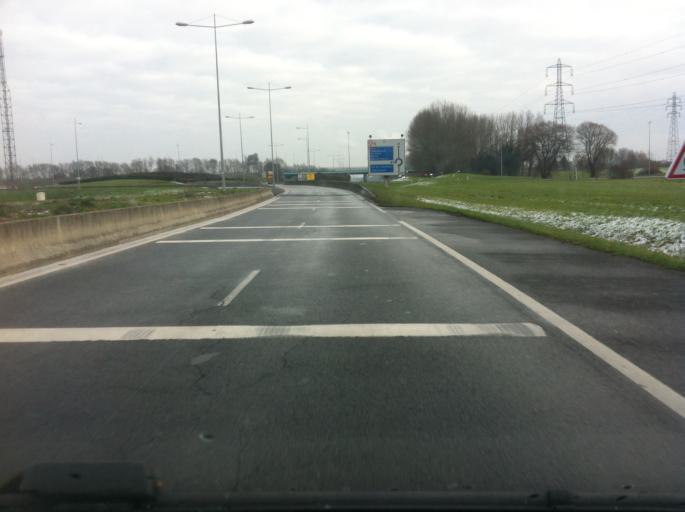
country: FR
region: Haute-Normandie
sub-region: Departement de la Seine-Maritime
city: Rogerville
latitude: 49.4792
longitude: 0.2596
